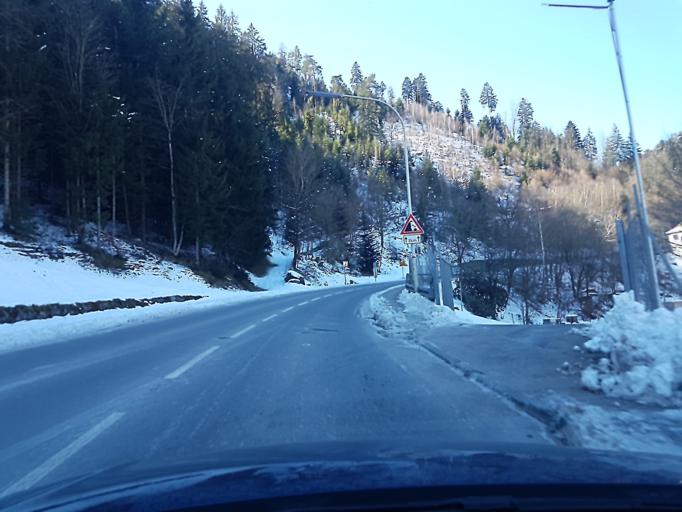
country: DE
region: Baden-Wuerttemberg
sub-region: Freiburg Region
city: Schramberg
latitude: 48.2211
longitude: 8.3777
